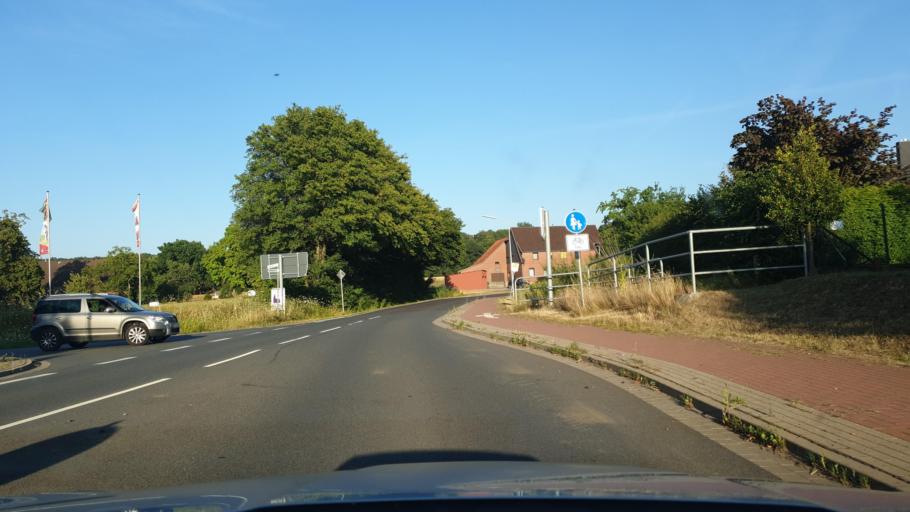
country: DE
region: Lower Saxony
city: Heuerssen
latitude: 52.3175
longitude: 9.2686
